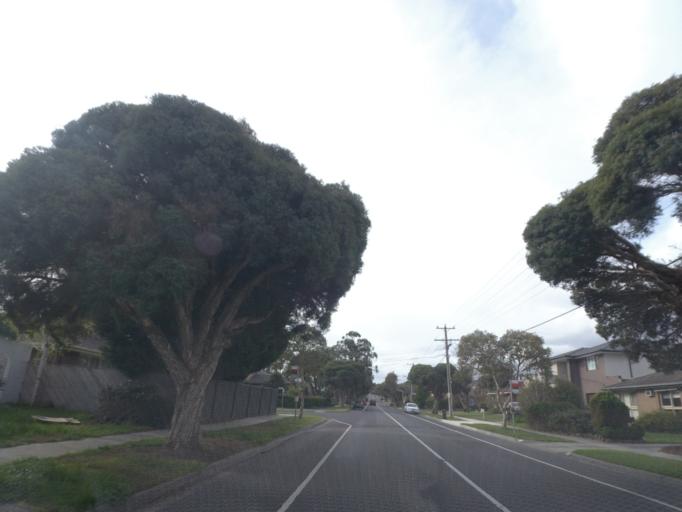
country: AU
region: Victoria
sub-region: Whitehorse
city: Vermont South
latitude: -37.8675
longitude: 145.1809
